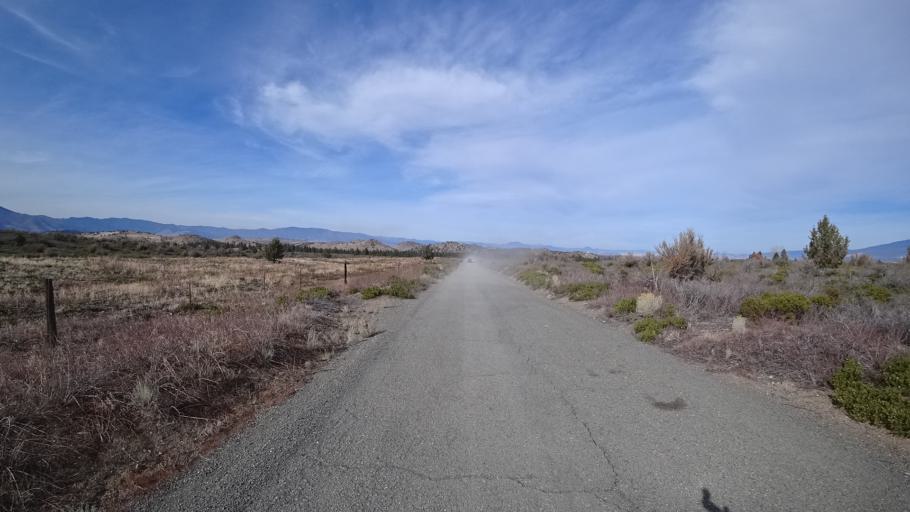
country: US
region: California
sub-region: Siskiyou County
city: Weed
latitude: 41.4834
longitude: -122.3650
